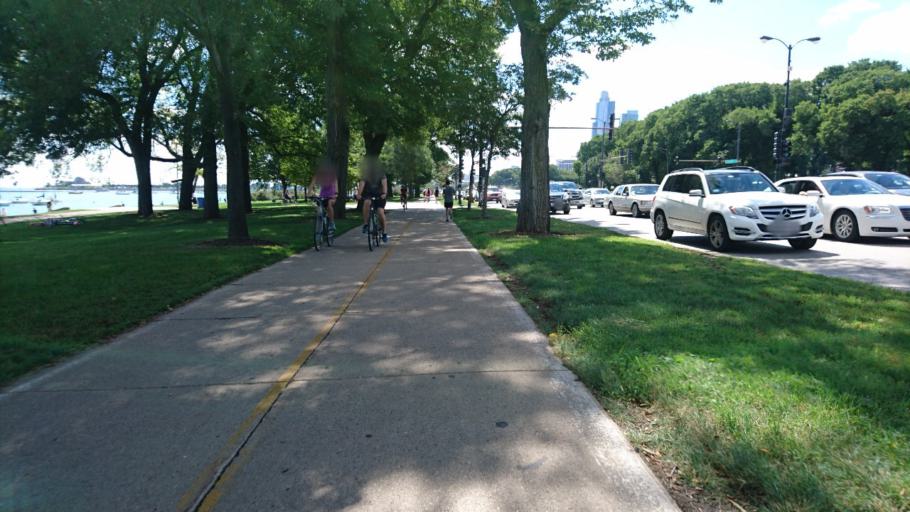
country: US
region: Illinois
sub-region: Cook County
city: Chicago
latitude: 41.8789
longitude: -87.6171
